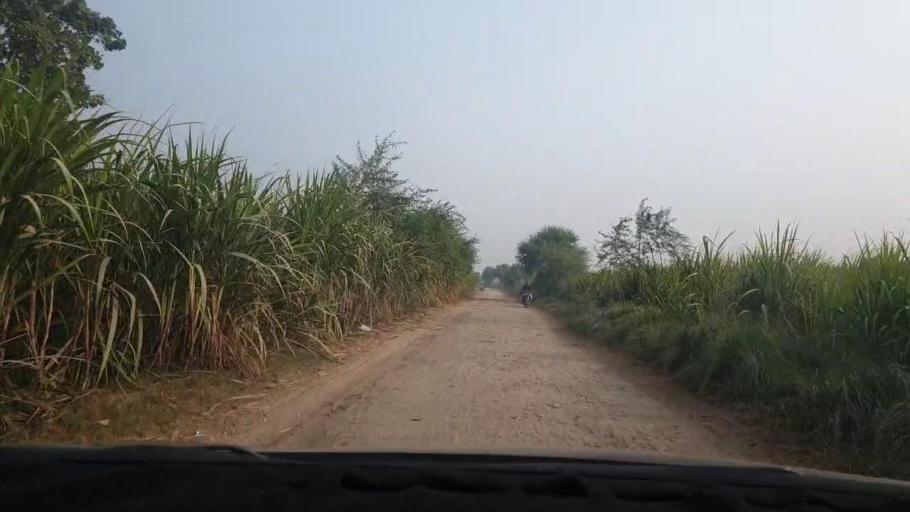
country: PK
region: Sindh
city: Matiari
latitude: 25.5740
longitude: 68.5108
